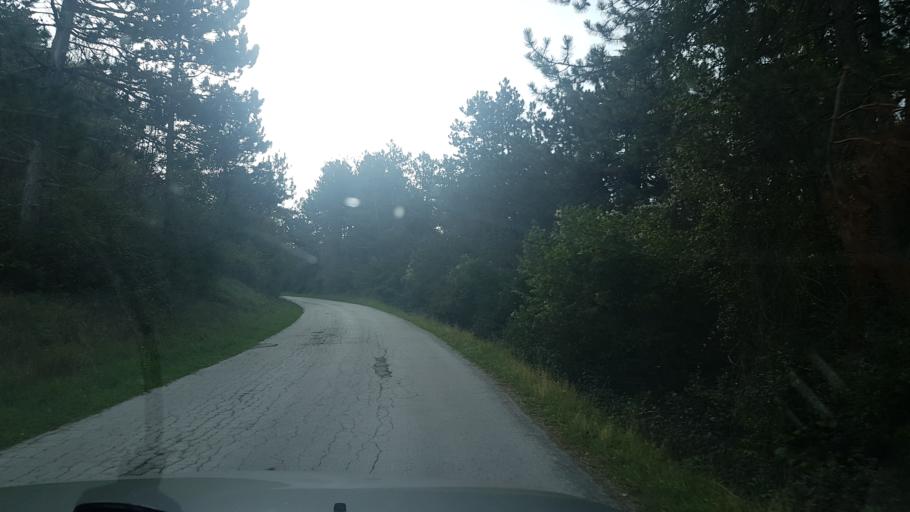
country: HR
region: Istarska
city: Buzet
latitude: 45.5000
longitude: 13.9956
